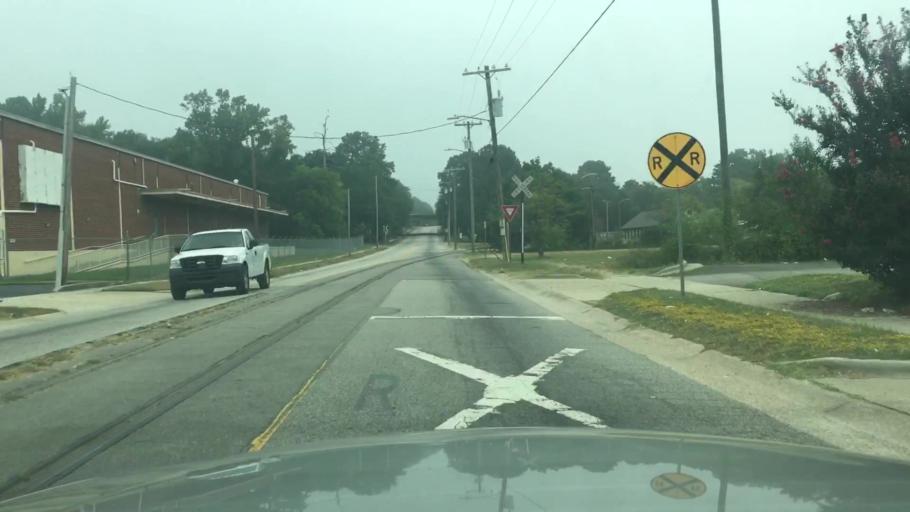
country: US
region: North Carolina
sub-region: Cumberland County
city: Fayetteville
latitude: 35.0662
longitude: -78.8839
